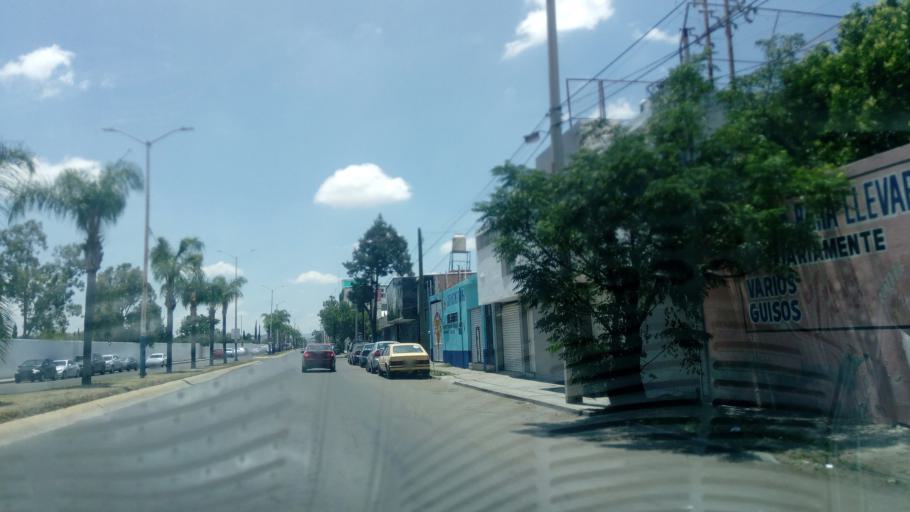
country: MX
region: Durango
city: Victoria de Durango
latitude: 24.0308
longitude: -104.6351
